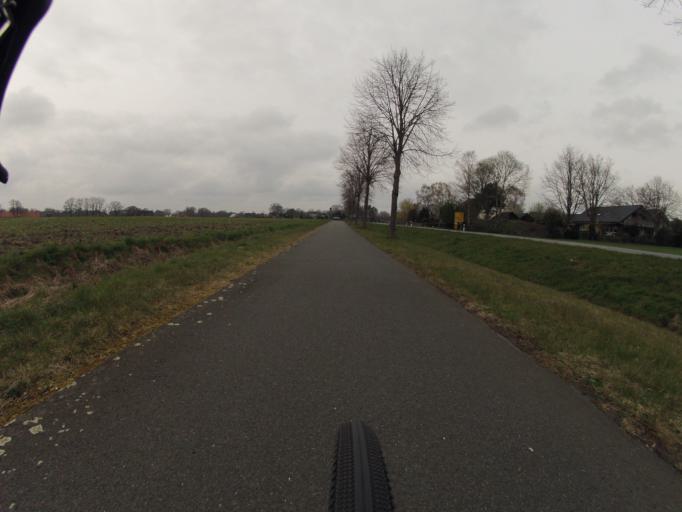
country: DE
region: North Rhine-Westphalia
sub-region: Regierungsbezirk Munster
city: Recke
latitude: 52.3484
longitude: 7.7300
